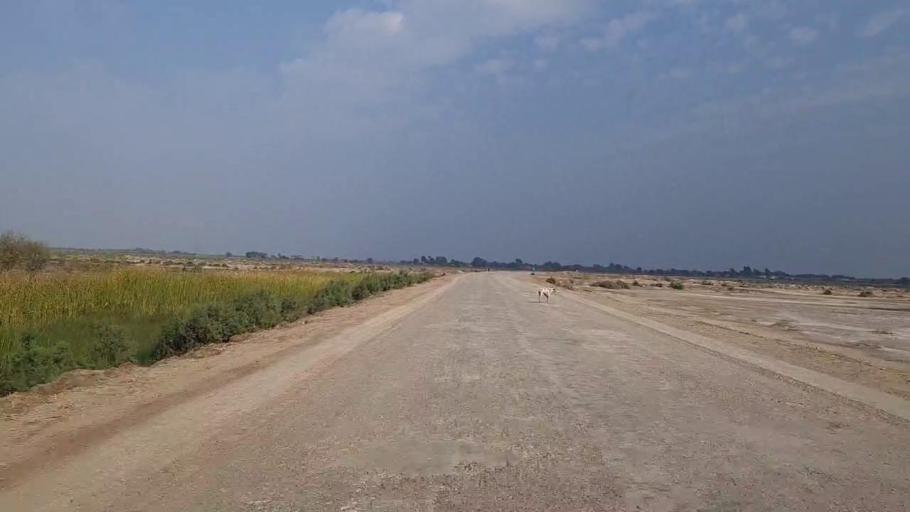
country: PK
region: Sindh
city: Mirwah Gorchani
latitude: 25.4045
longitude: 69.0579
